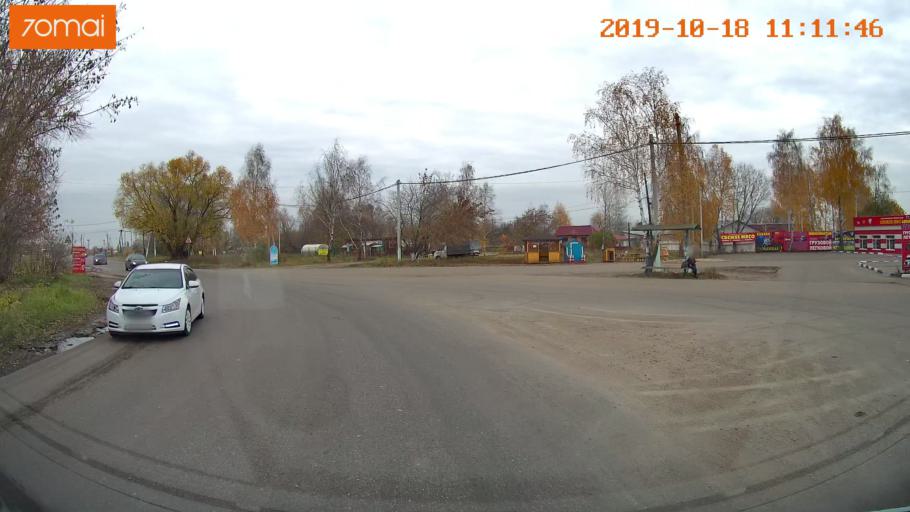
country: RU
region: Tula
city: Kimovsk
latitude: 53.9613
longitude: 38.5518
